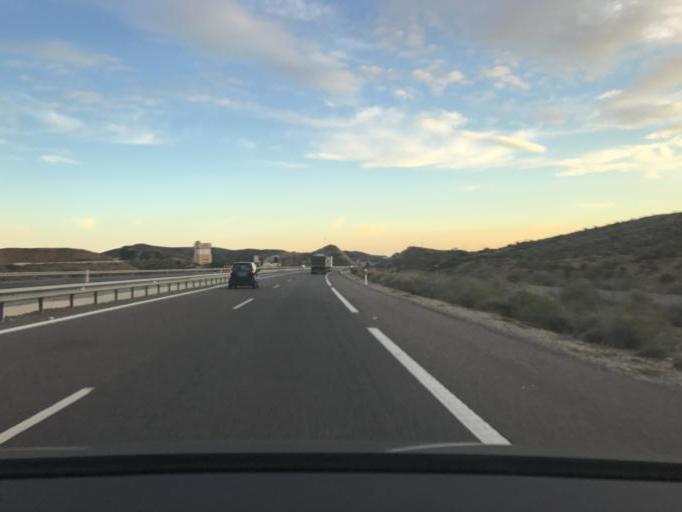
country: ES
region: Andalusia
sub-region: Provincia de Almeria
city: Rioja
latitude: 36.9423
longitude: -2.4501
